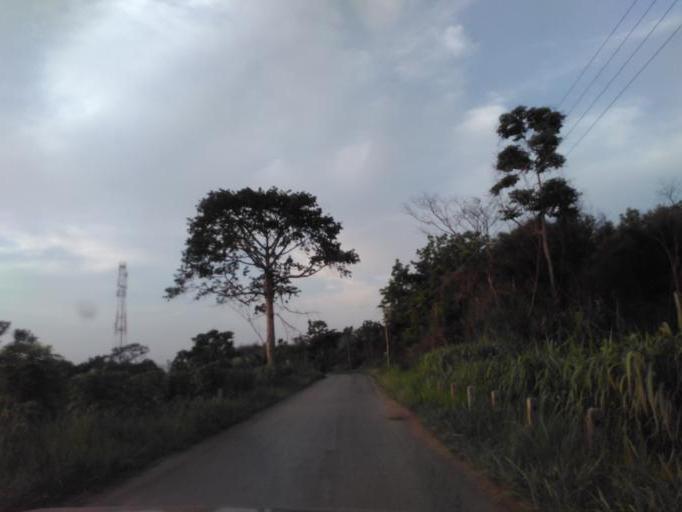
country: GH
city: Bekwai
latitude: 6.5410
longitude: -1.4403
